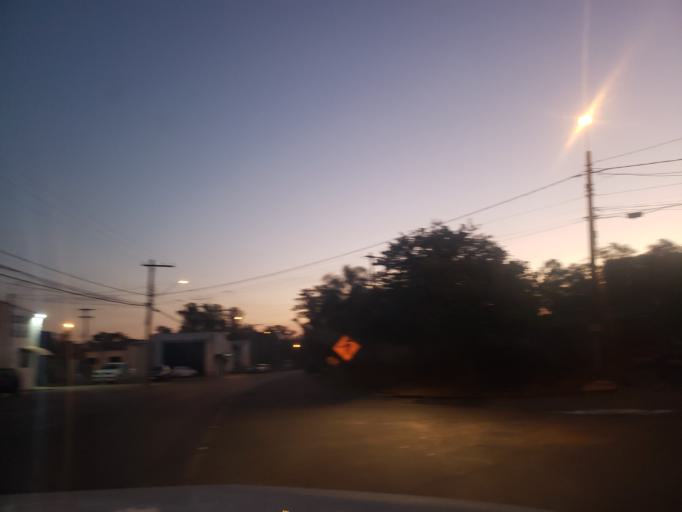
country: BR
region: Sao Paulo
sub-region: Conchal
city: Conchal
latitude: -22.2971
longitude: -47.1313
